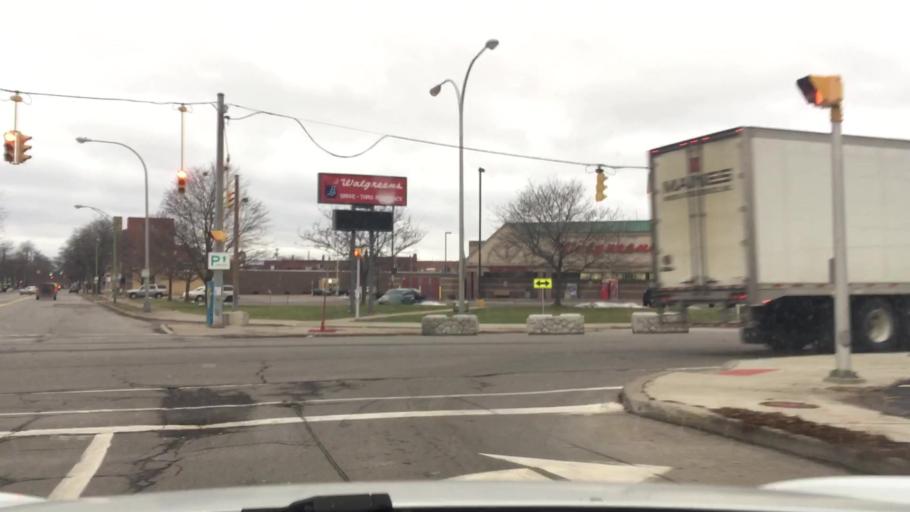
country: US
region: New York
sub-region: Erie County
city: Tonawanda
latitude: 43.0196
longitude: -78.8748
